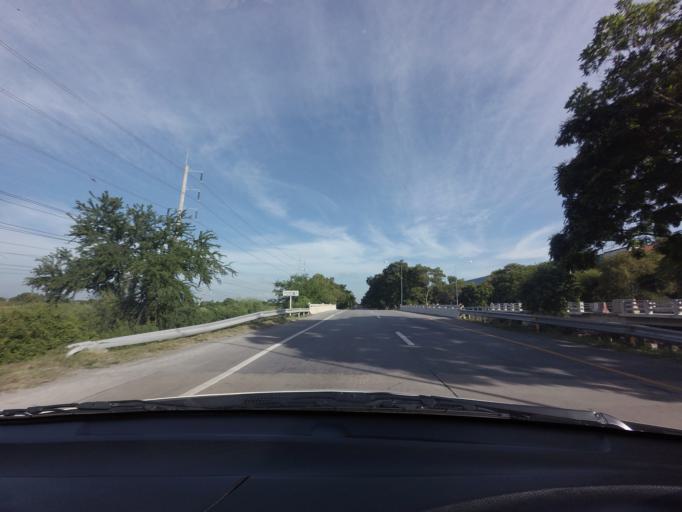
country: TH
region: Suphan Buri
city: Bang Pla Ma
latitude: 14.3587
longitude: 100.1853
